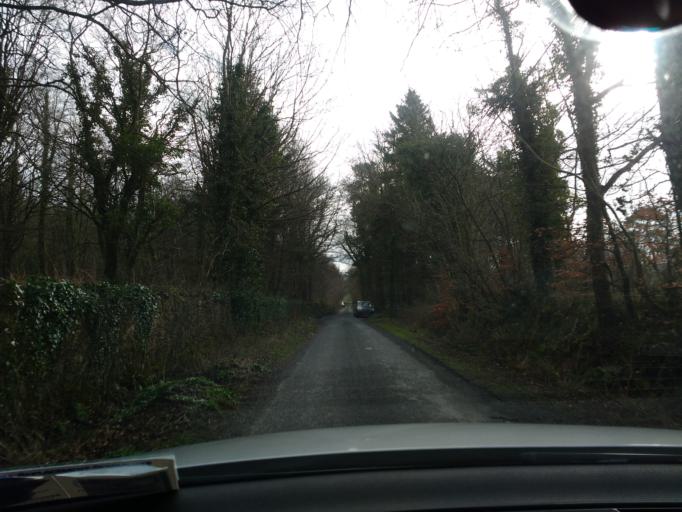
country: IE
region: Leinster
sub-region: Laois
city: Rathdowney
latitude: 52.6635
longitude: -7.5642
